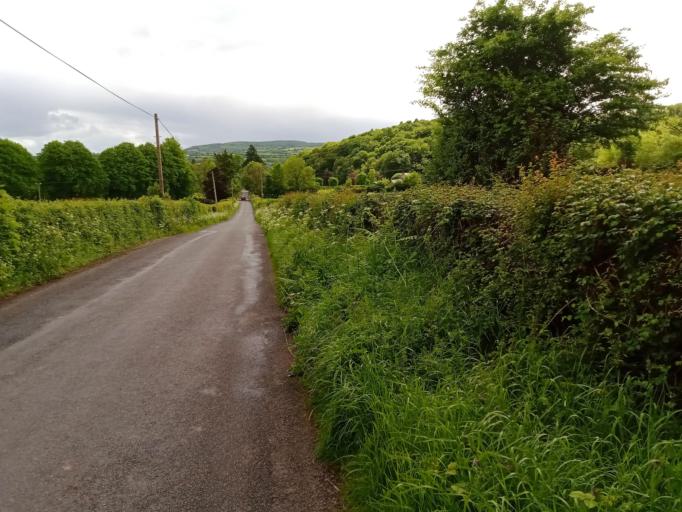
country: IE
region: Leinster
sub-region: Kilkenny
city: Thomastown
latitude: 52.4977
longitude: -7.1234
